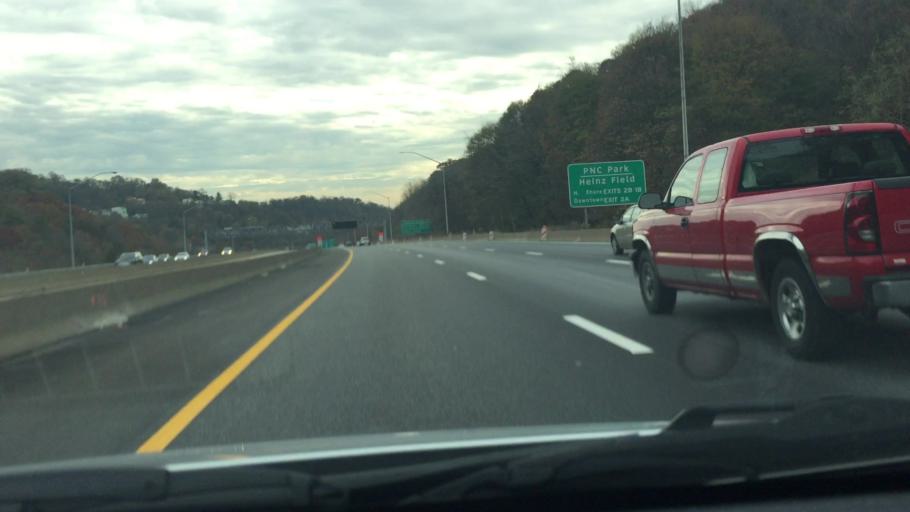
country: US
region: Pennsylvania
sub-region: Allegheny County
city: Millvale
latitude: 40.4728
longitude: -80.0053
